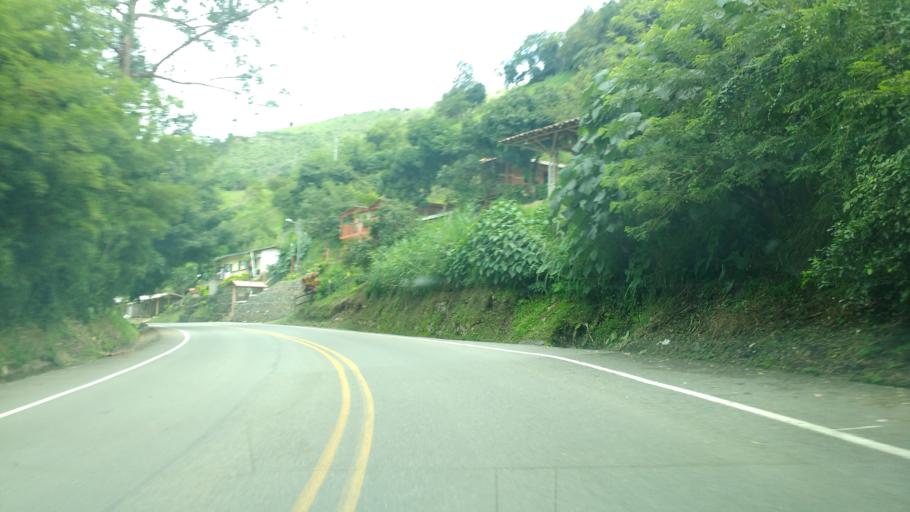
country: CO
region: Antioquia
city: Amaga
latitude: 6.0597
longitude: -75.7421
